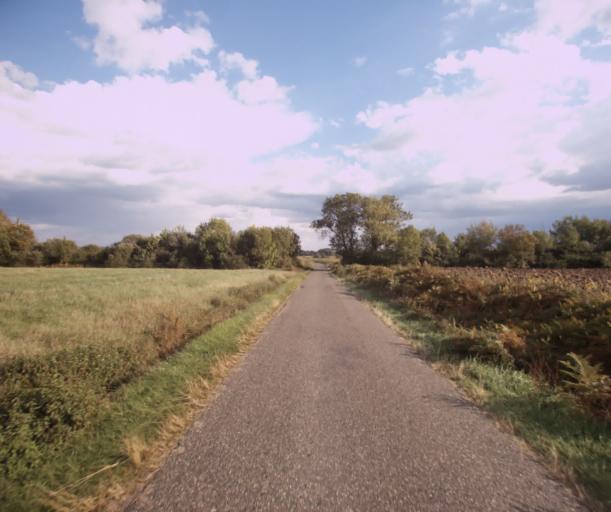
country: FR
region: Midi-Pyrenees
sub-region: Departement du Gers
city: Cazaubon
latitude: 43.9110
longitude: -0.0639
